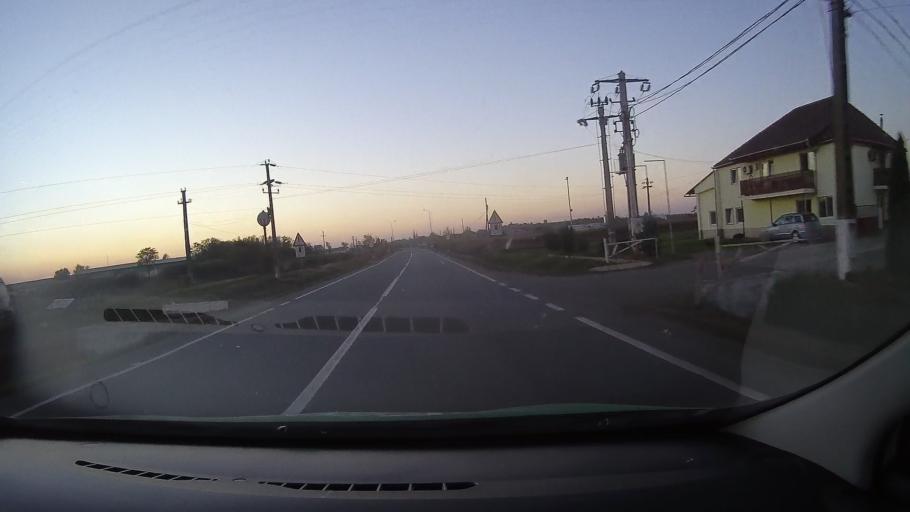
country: RO
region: Bihor
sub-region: Comuna Tarcea
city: Tarcea
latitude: 47.4529
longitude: 22.1815
